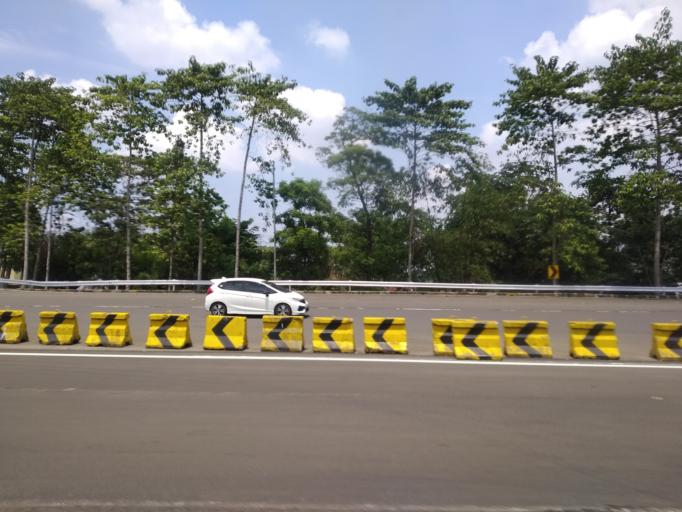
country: ID
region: West Java
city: Bogor
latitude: -6.5970
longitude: 106.8190
